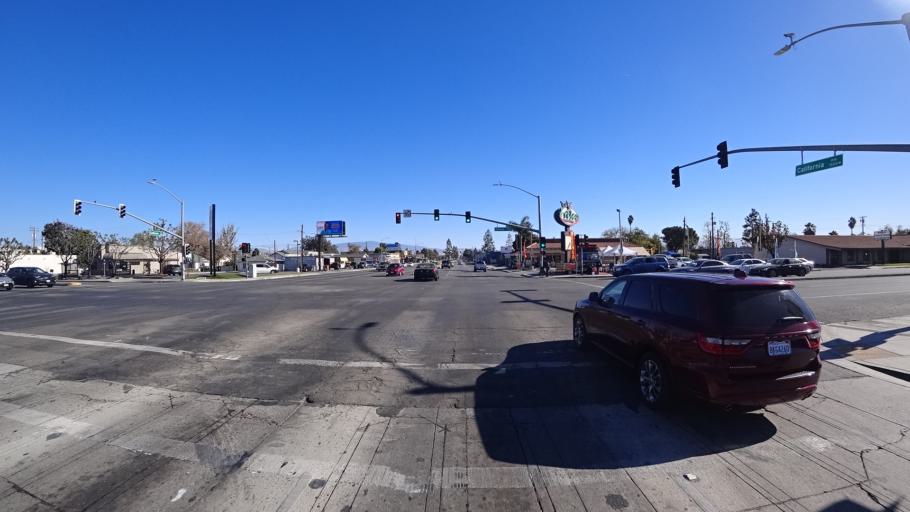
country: US
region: California
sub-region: Kern County
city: Bakersfield
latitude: 35.3684
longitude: -119.0190
